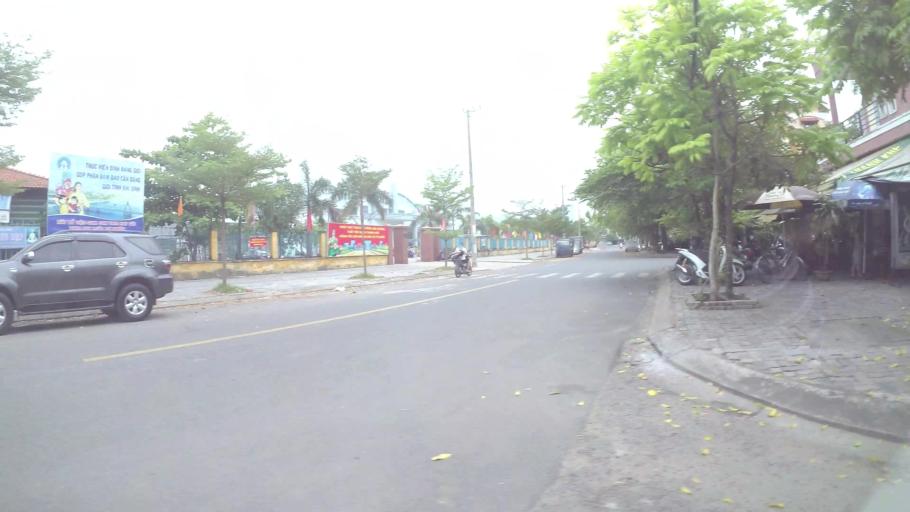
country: VN
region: Da Nang
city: Thanh Khe
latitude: 16.0632
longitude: 108.1829
